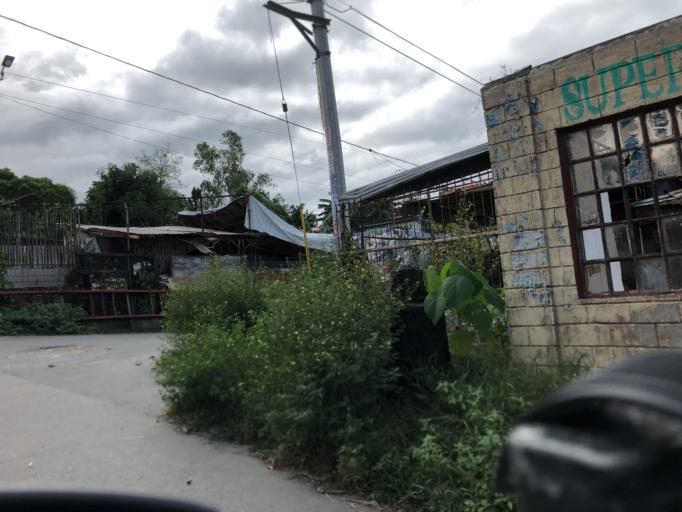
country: PH
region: Central Luzon
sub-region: Province of Bulacan
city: San Jose del Monte
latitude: 14.7603
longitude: 121.0512
